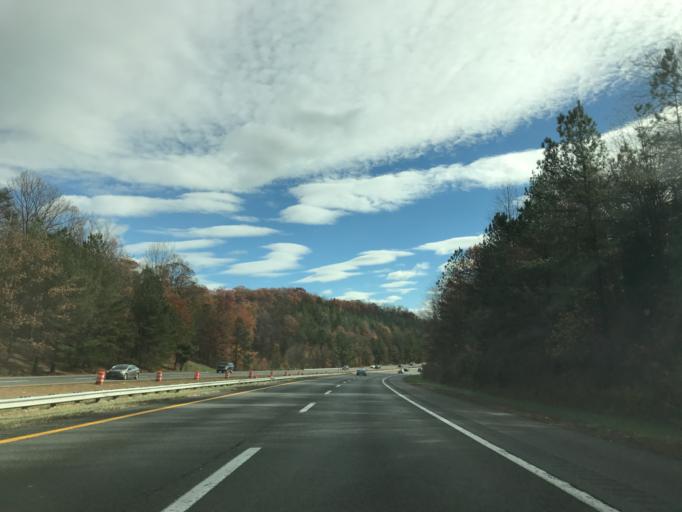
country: US
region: Maryland
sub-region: Anne Arundel County
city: Crownsville
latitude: 39.0060
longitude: -76.6034
